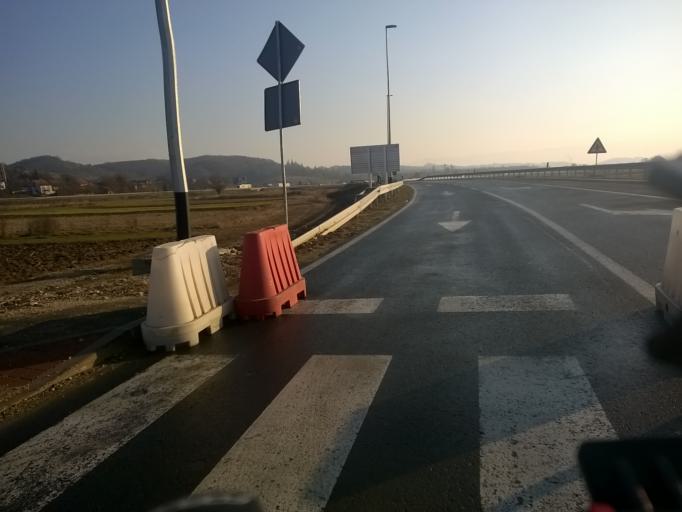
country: HR
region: Krapinsko-Zagorska
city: Zabok
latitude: 46.0764
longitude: 15.9138
